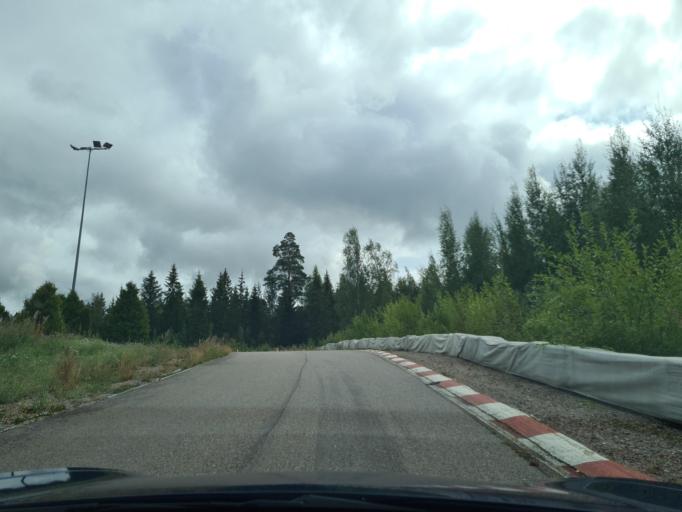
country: FI
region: Uusimaa
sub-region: Helsinki
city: Pornainen
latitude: 60.3445
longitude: 25.4272
